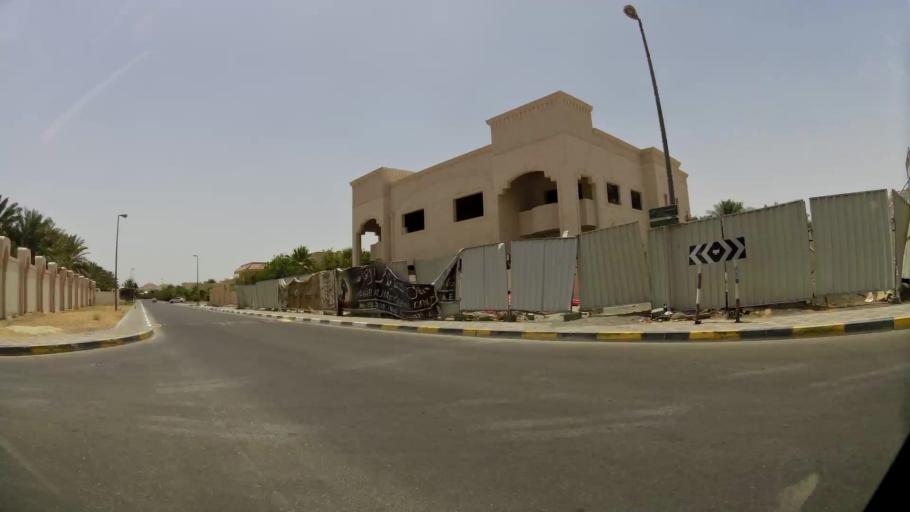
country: AE
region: Abu Dhabi
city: Al Ain
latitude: 24.1929
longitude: 55.7329
